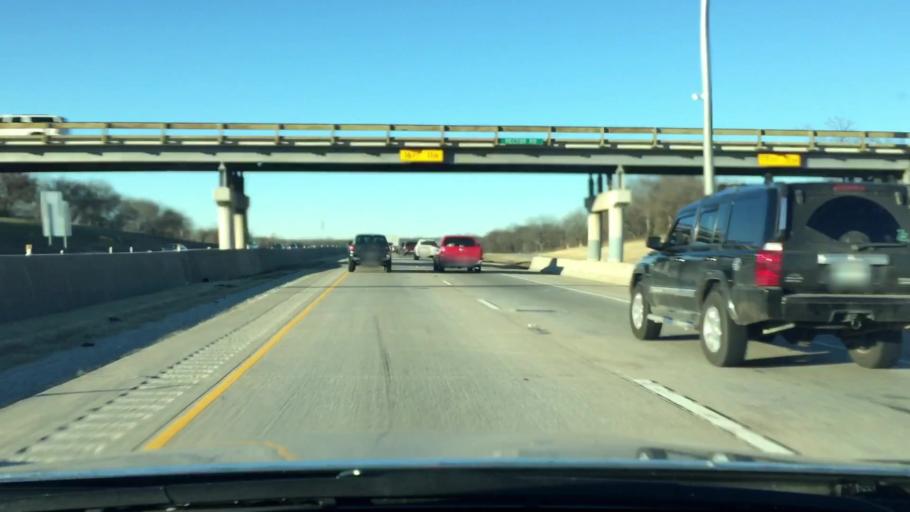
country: US
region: Texas
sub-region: Denton County
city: Sanger
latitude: 33.3244
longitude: -97.1804
